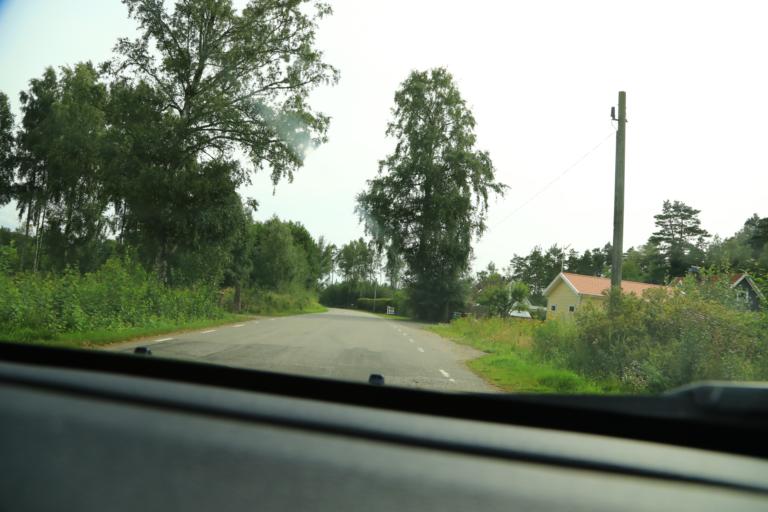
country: SE
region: Halland
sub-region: Varbergs Kommun
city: Varberg
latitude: 57.1779
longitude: 12.2219
